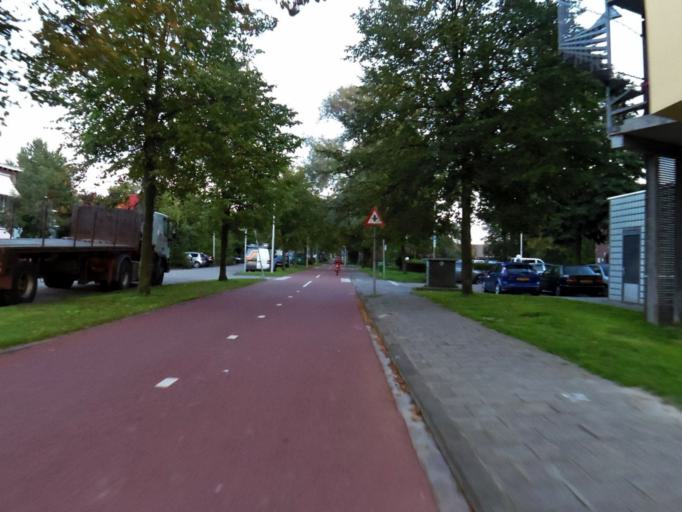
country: NL
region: South Holland
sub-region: Gemeente Oegstgeest
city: Oegstgeest
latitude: 52.1587
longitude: 4.4501
